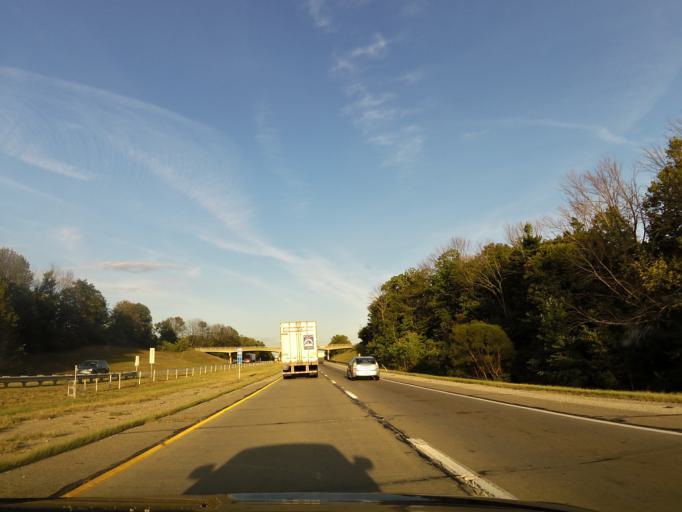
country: US
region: Indiana
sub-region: Boone County
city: Zionsville
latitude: 39.9316
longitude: -86.3240
